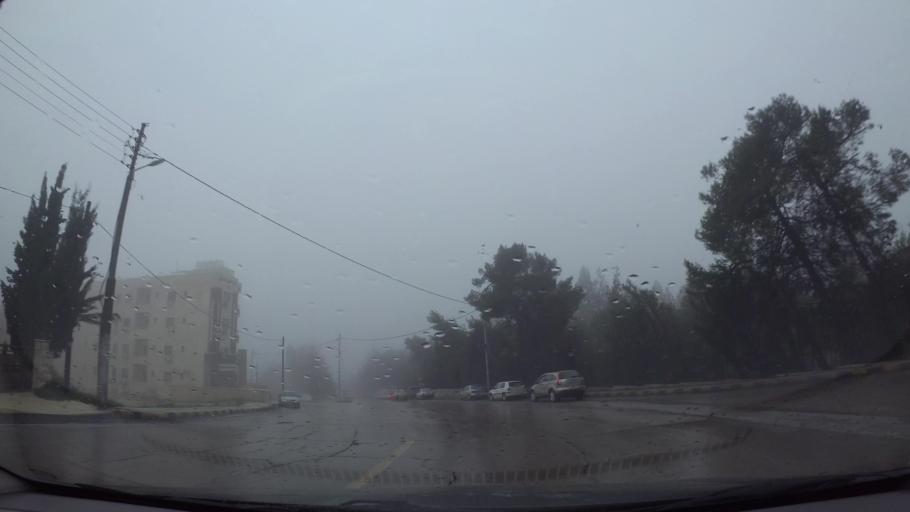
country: JO
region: Amman
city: Al Jubayhah
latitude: 32.0175
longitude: 35.8750
